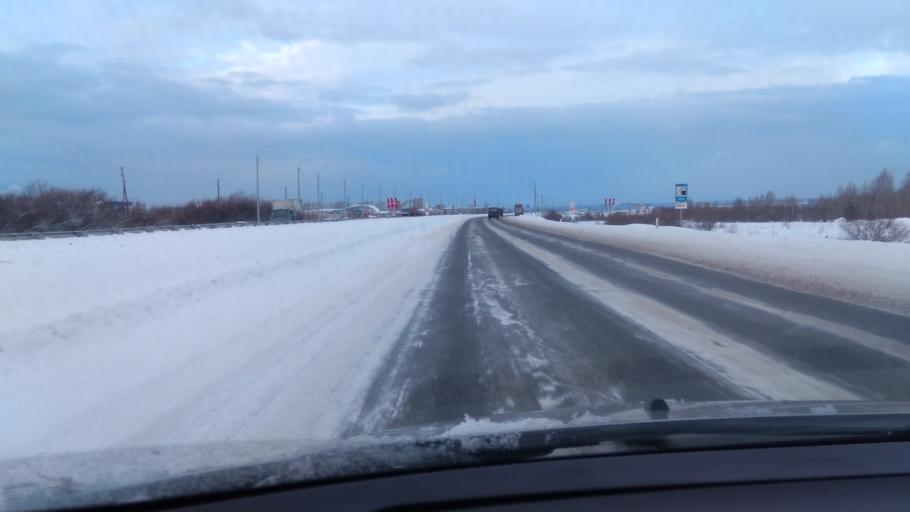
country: RU
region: Sverdlovsk
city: Tsementnyy
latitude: 57.4638
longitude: 60.1871
